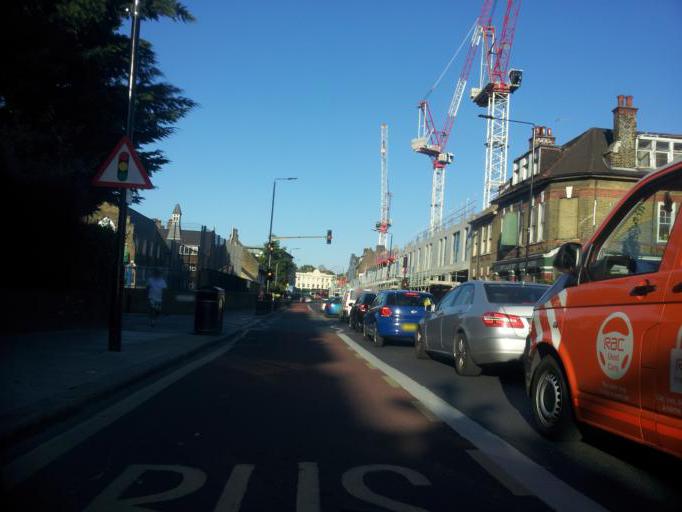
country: GB
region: England
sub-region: Greater London
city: Blackheath
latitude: 51.4814
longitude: -0.0138
